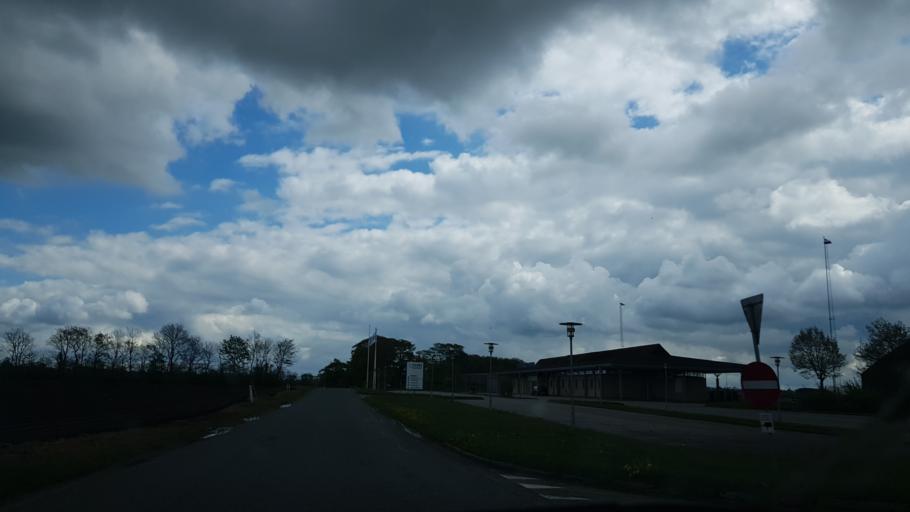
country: DK
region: South Denmark
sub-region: Haderslev Kommune
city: Vojens
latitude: 55.2227
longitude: 9.2895
